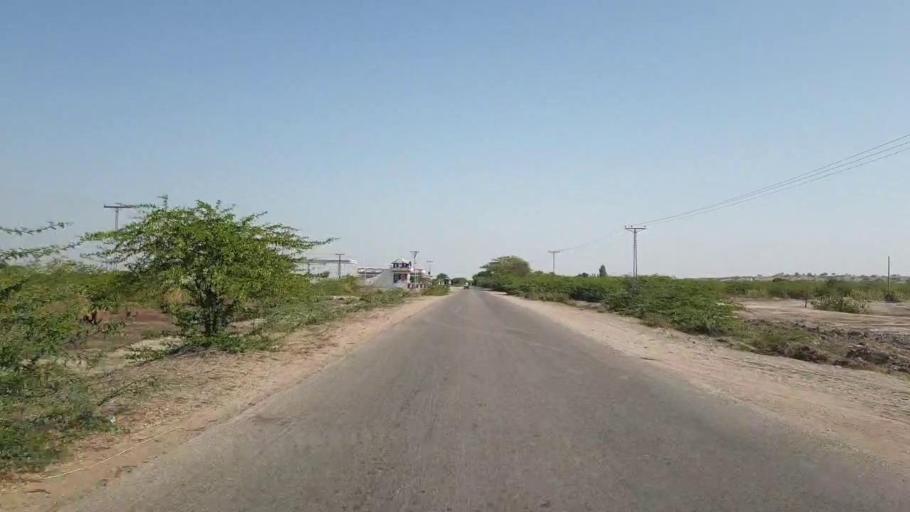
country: PK
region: Sindh
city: Chor
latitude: 25.4819
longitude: 69.7779
